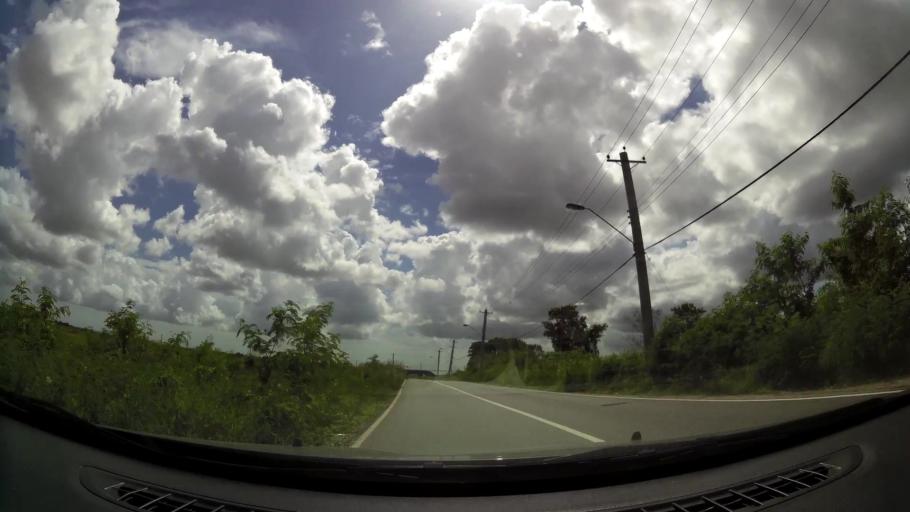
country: TT
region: City of San Fernando
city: San Fernando
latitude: 10.2432
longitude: -61.4987
